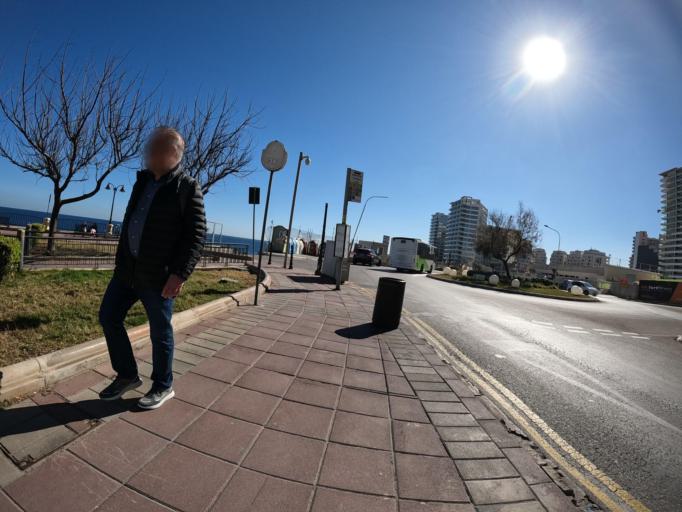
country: MT
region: Tas-Sliema
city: Sliema
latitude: 35.9100
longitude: 14.5100
